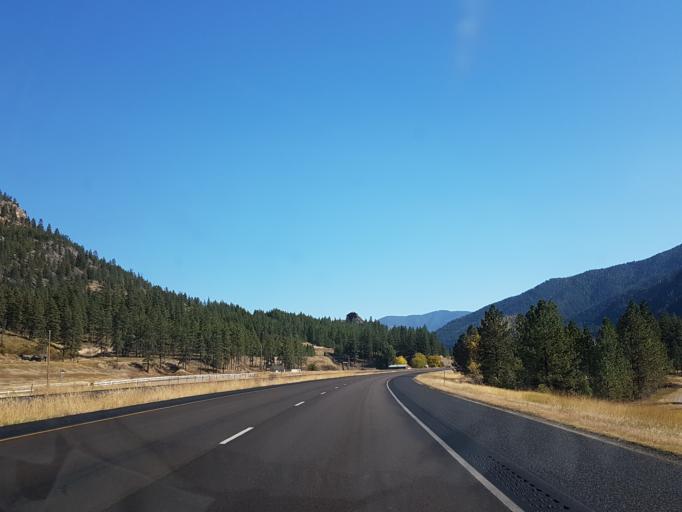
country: US
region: Montana
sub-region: Missoula County
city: Frenchtown
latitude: 47.0163
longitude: -114.5078
